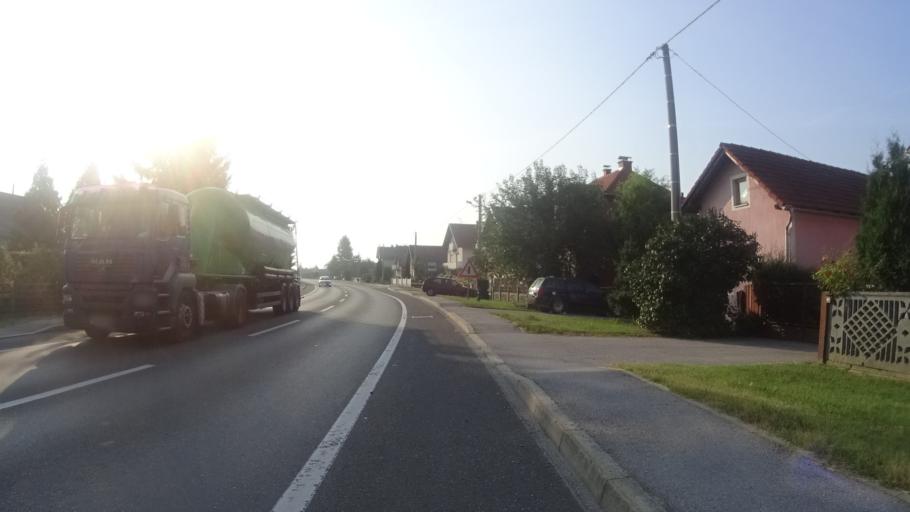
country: HR
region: Varazdinska
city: Sracinec
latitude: 46.3365
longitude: 16.2538
